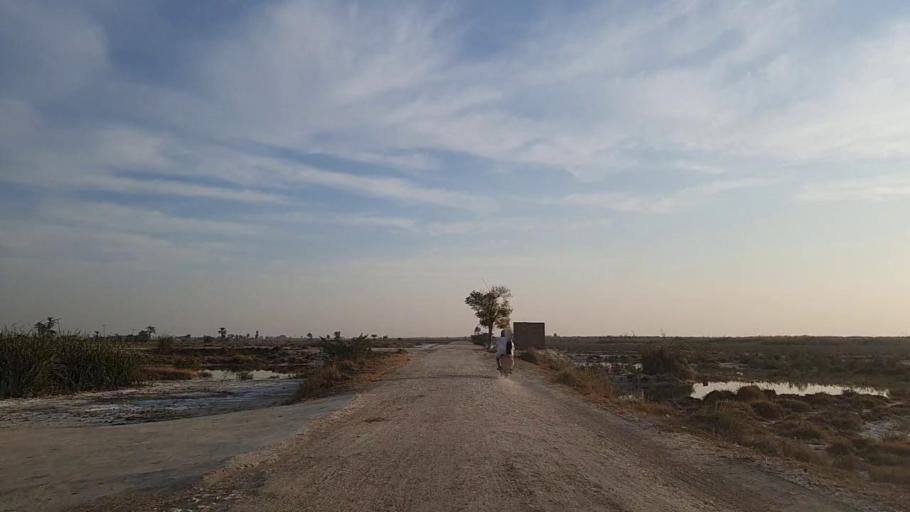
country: PK
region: Sindh
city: Bandhi
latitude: 26.5824
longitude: 68.3334
